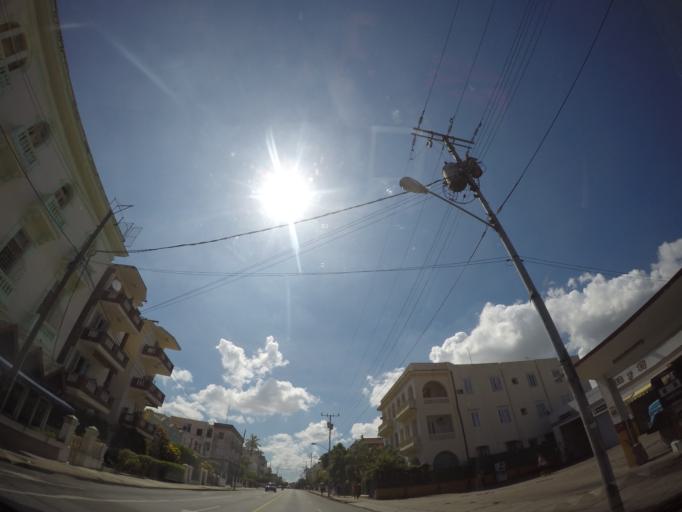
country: CU
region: La Habana
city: Guanabacoa
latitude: 23.0957
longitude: -82.3166
